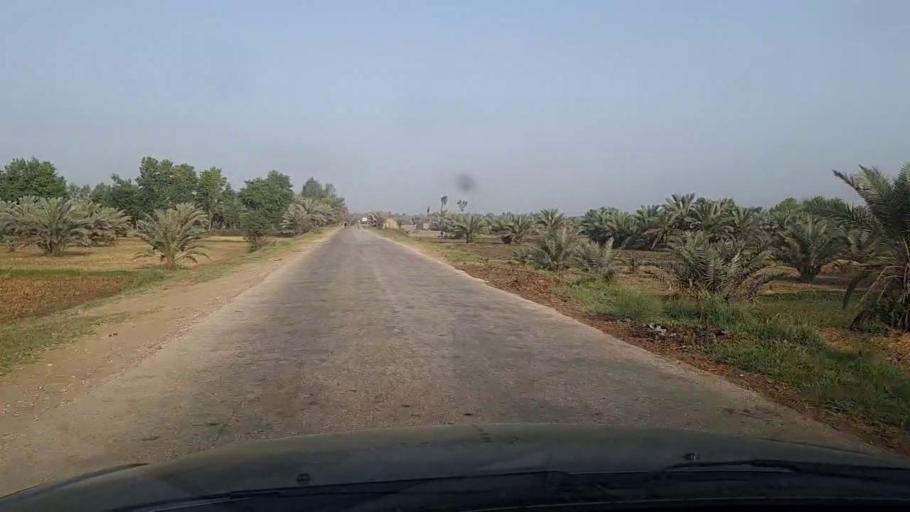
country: PK
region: Sindh
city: Pir jo Goth
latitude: 27.5541
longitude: 68.6841
